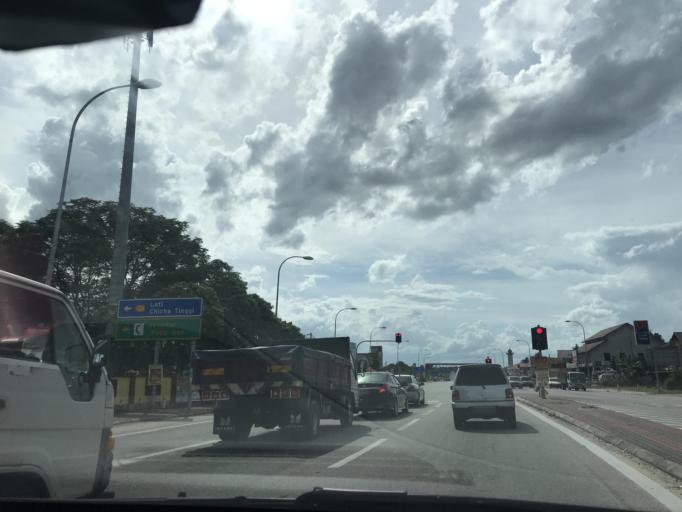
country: MY
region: Kelantan
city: Kampung Lemal
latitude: 6.0246
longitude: 102.1470
